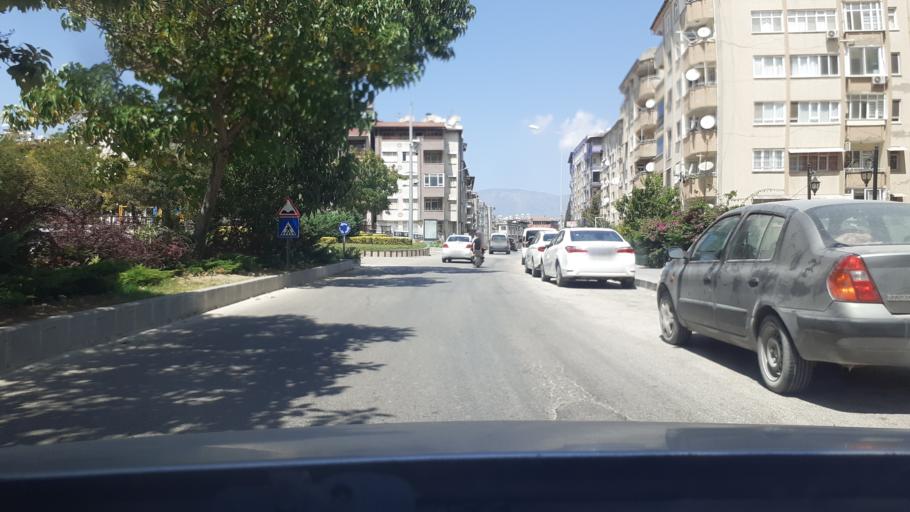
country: TR
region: Hatay
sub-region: Antakya Ilcesi
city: Antakya
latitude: 36.1961
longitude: 36.1558
